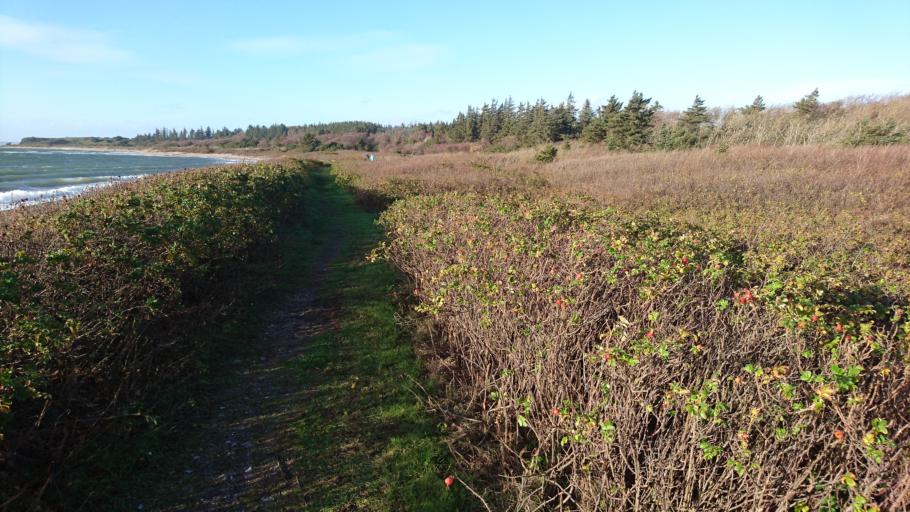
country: DK
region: North Denmark
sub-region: Morso Kommune
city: Nykobing Mors
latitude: 56.8280
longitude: 8.9652
